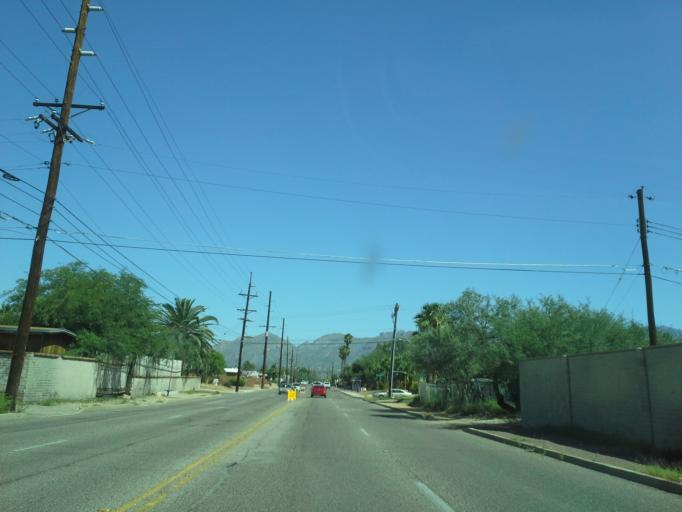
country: US
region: Arizona
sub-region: Pima County
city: Tucson
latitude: 32.2461
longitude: -110.9268
